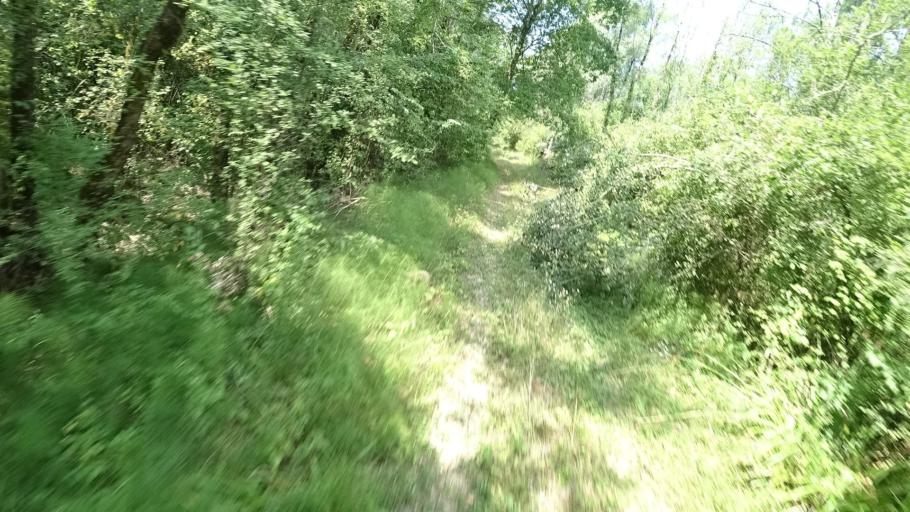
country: HR
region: Istarska
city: Karojba
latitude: 45.3464
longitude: 13.8585
